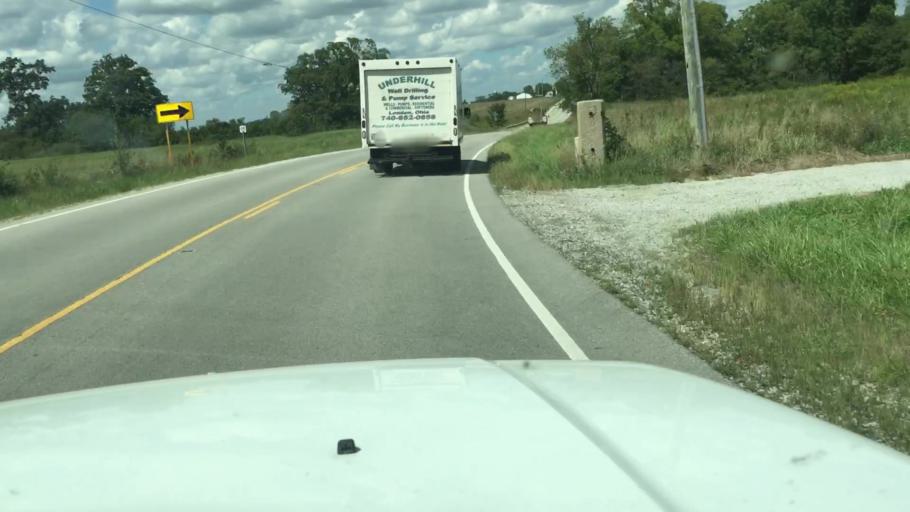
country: US
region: Ohio
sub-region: Madison County
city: Bethel
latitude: 39.8154
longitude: -83.3535
